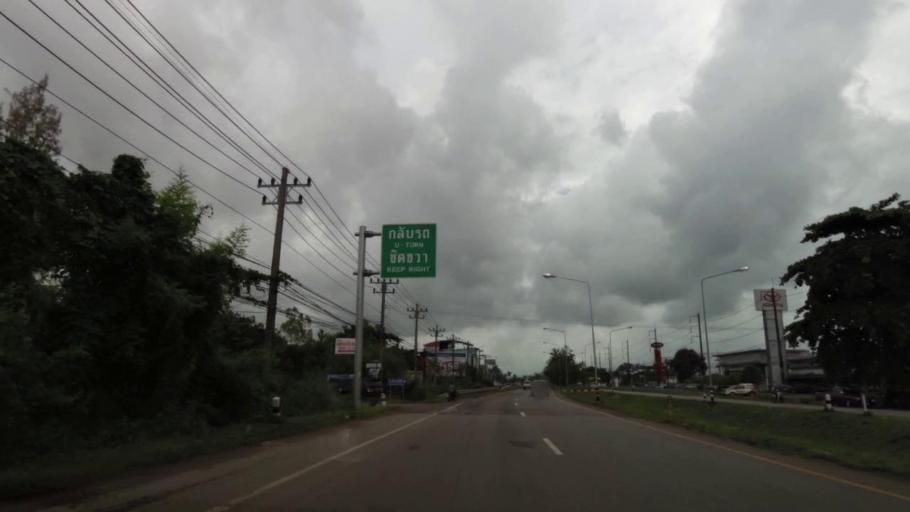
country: TH
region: Chanthaburi
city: Chanthaburi
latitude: 12.5964
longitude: 102.1423
